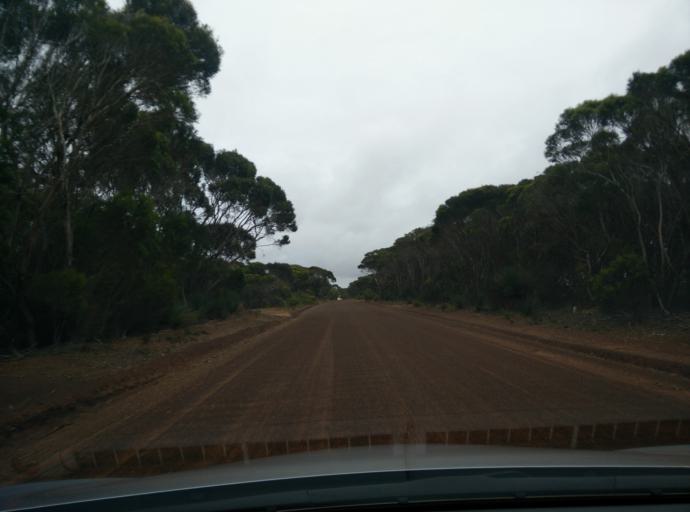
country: AU
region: South Australia
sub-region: Kangaroo Island
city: Kingscote
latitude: -35.8526
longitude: 137.4809
